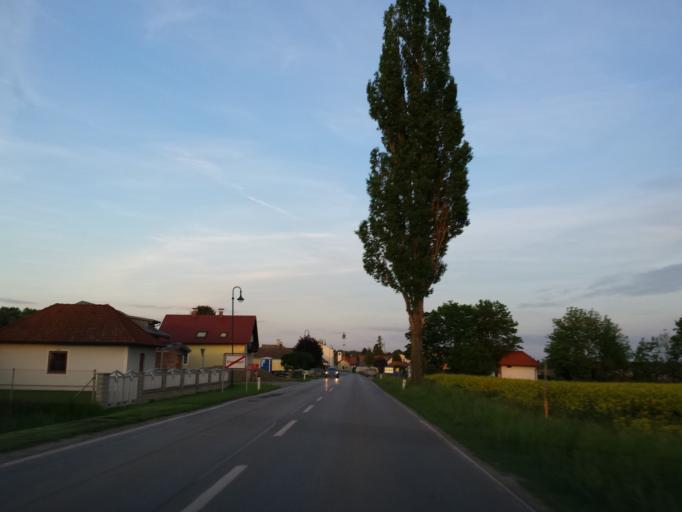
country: AT
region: Lower Austria
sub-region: Politischer Bezirk Tulln
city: Michelhausen
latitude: 48.3399
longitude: 15.9295
